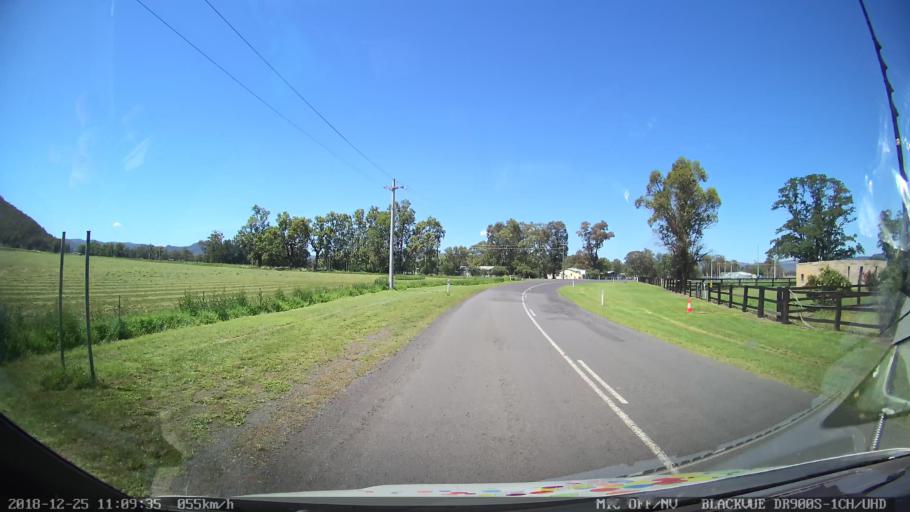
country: AU
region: New South Wales
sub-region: Upper Hunter Shire
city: Merriwa
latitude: -32.4125
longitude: 150.1182
